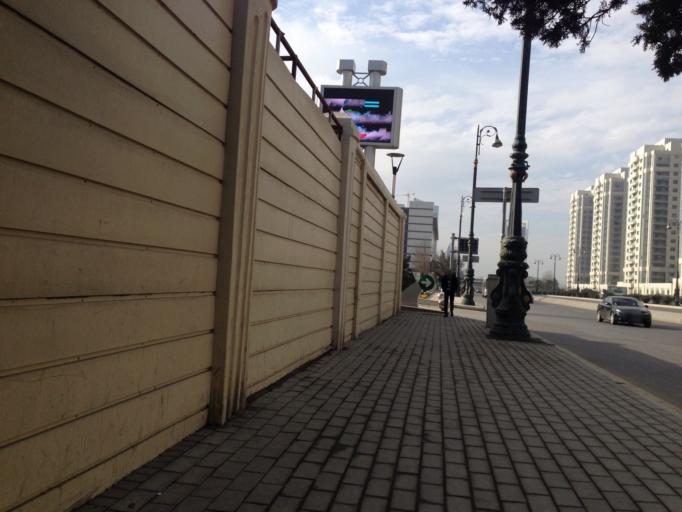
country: AZ
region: Baki
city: Sabuncu
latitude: 40.4189
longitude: 49.9129
